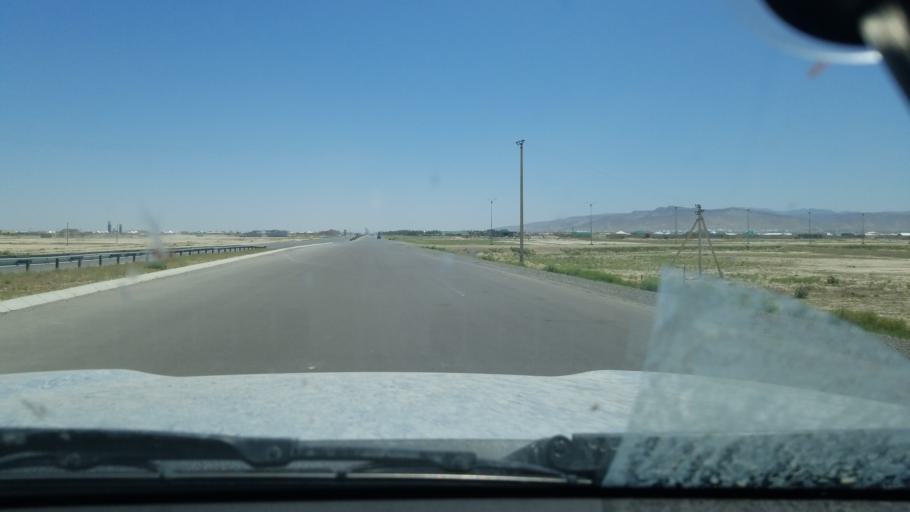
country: TM
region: Balkan
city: Serdar
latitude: 39.0085
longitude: 56.2423
